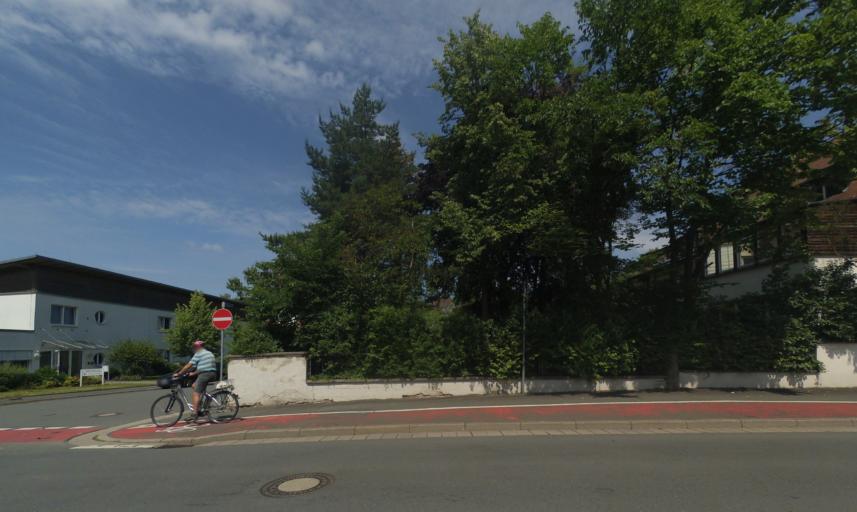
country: DE
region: Bavaria
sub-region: Upper Franconia
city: Kulmbach
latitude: 50.1026
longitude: 11.4469
